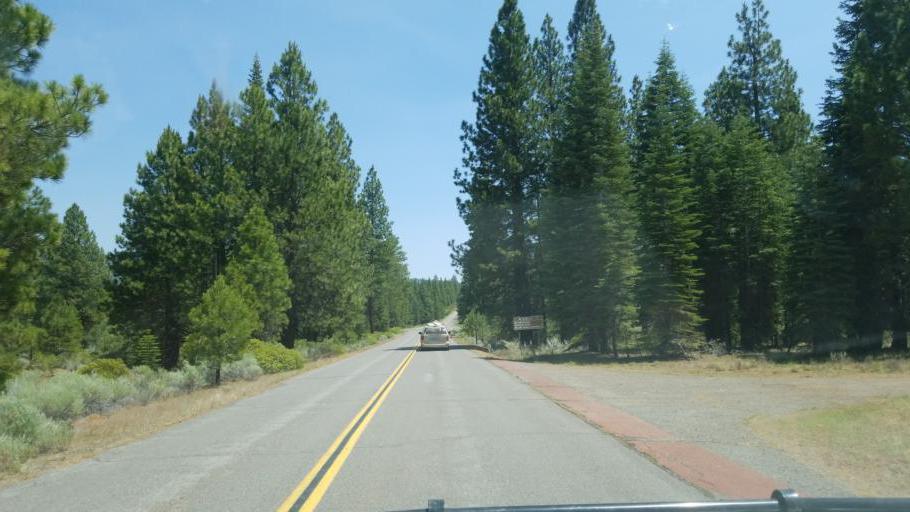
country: US
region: California
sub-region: Lassen County
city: Susanville
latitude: 40.5440
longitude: -120.7988
